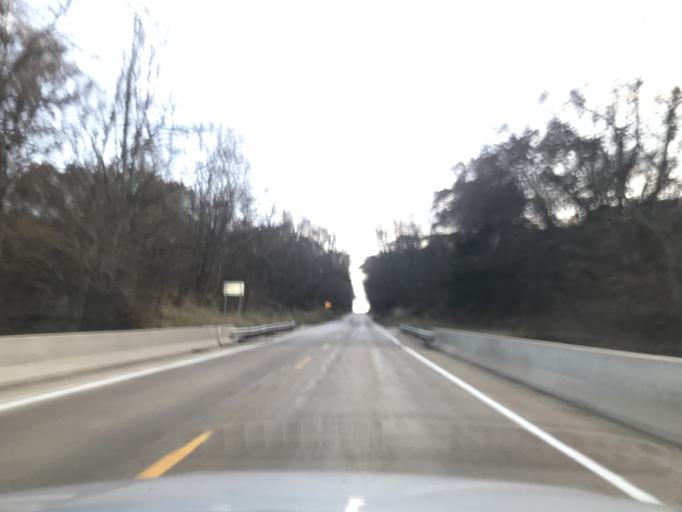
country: US
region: Illinois
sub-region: Henderson County
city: Oquawka
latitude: 41.0018
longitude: -90.8536
